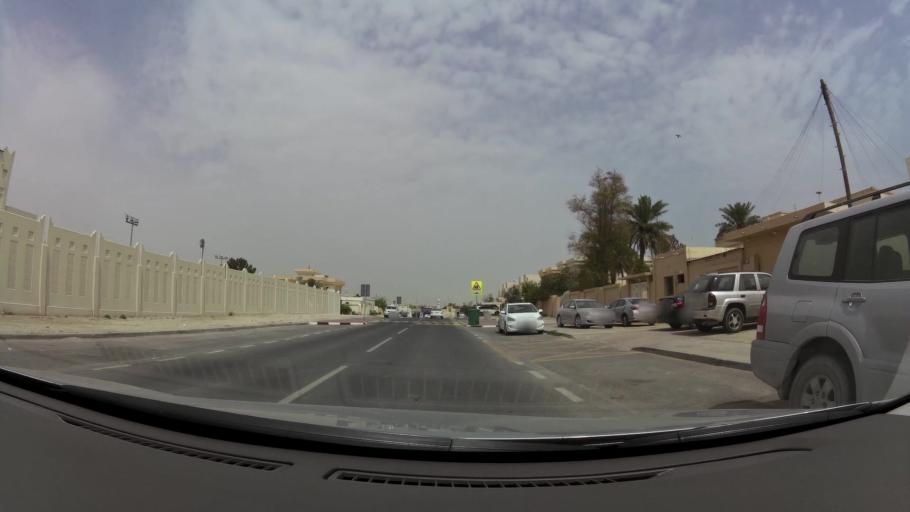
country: QA
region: Baladiyat ad Dawhah
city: Doha
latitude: 25.3091
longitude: 51.4768
